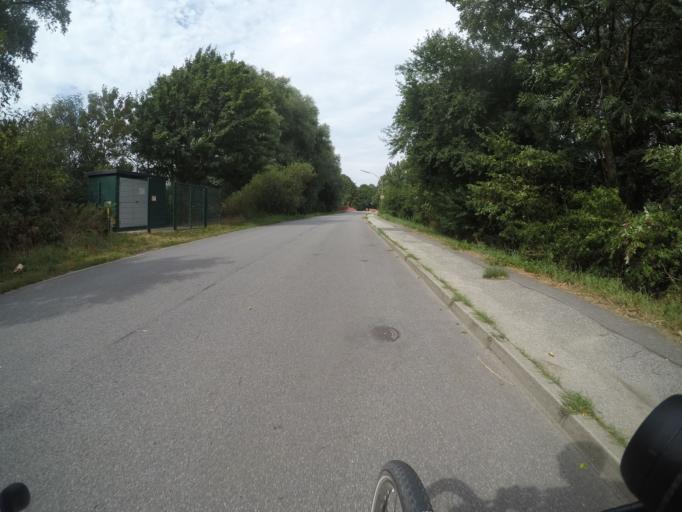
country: DE
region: Schleswig-Holstein
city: Oststeinbek
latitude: 53.4806
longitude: 10.1282
